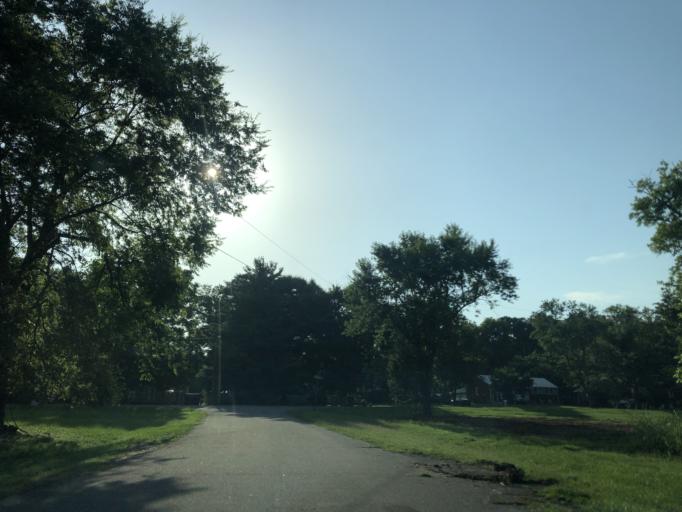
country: US
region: Tennessee
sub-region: Davidson County
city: Lakewood
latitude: 36.1463
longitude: -86.6580
